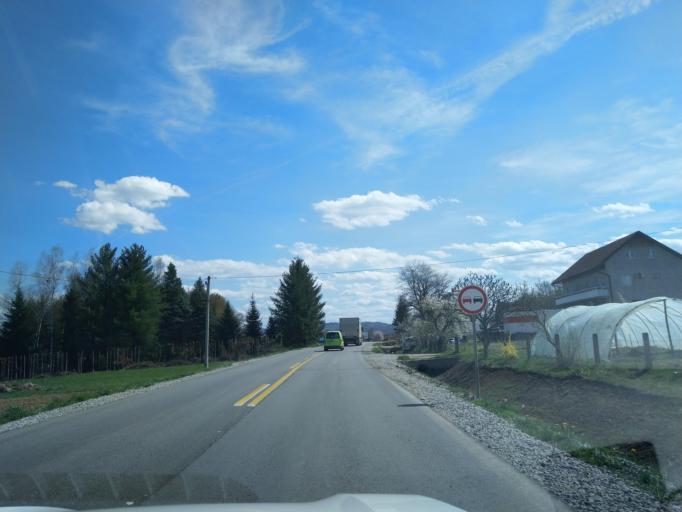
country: RS
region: Central Serbia
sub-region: Zlatiborski Okrug
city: Pozega
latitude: 43.8199
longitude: 20.0851
